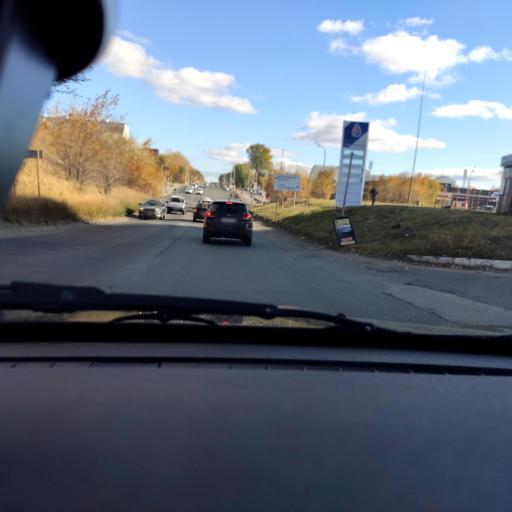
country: RU
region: Samara
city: Tol'yatti
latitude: 53.5087
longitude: 49.2531
